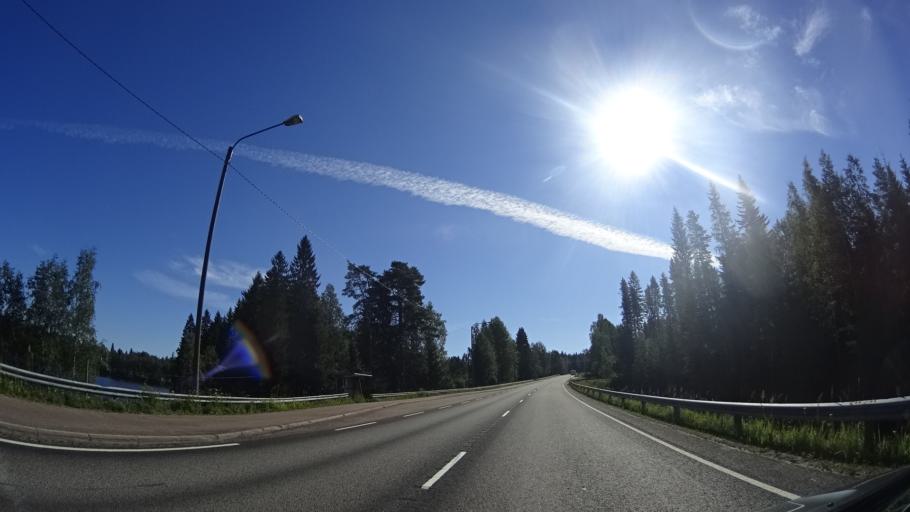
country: FI
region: Central Finland
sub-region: Jyvaeskylae
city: Petaejaevesi
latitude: 62.2715
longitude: 25.3166
